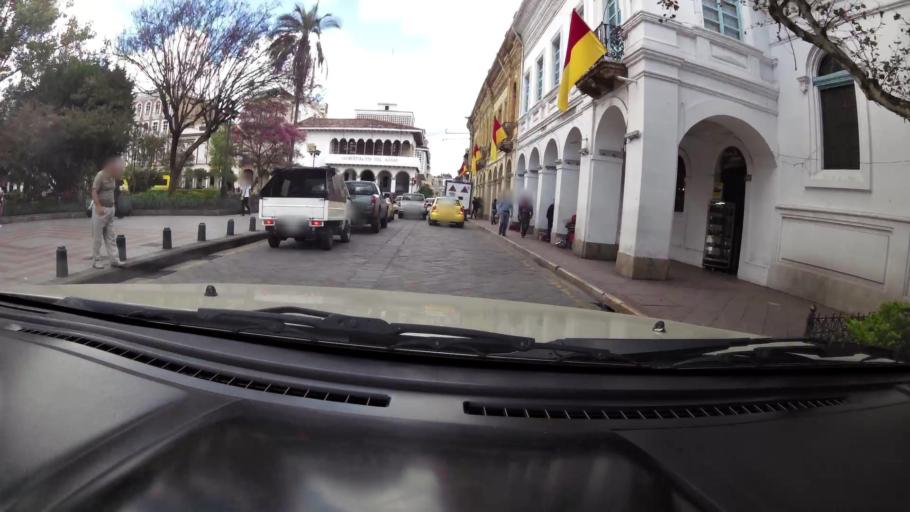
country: EC
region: Azuay
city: Cuenca
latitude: -2.8975
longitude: -79.0041
